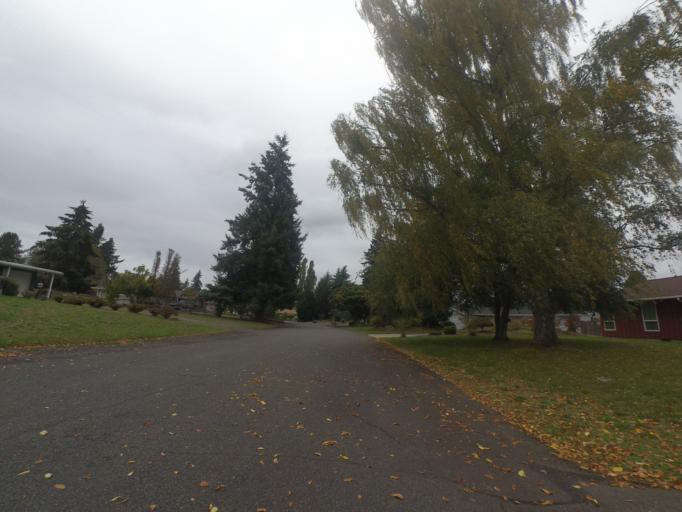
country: US
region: Washington
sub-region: Pierce County
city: McChord Air Force Base
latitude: 47.1515
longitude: -122.5068
